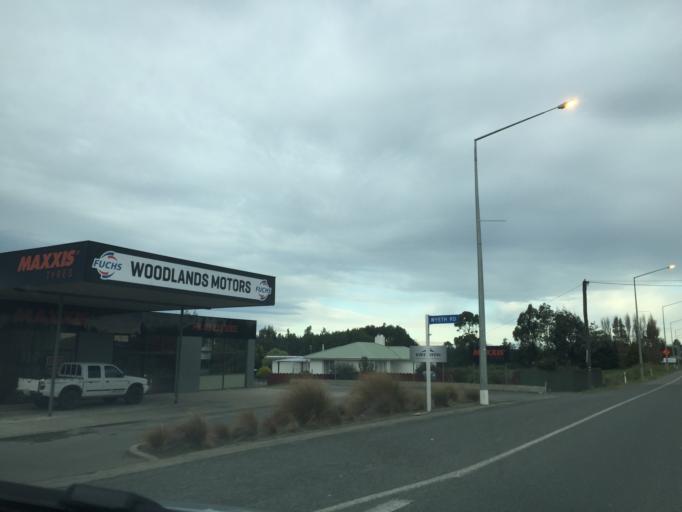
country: NZ
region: Southland
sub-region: Invercargill City
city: Invercargill
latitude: -46.3555
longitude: 168.5506
